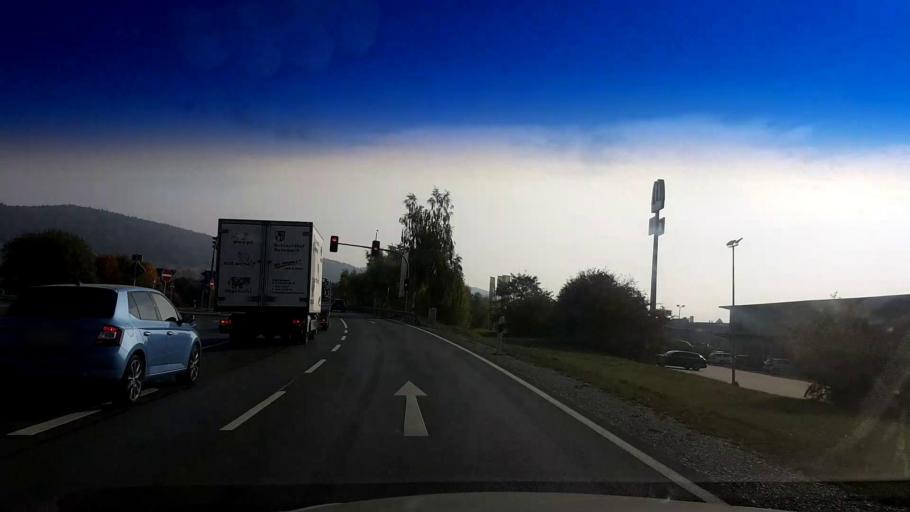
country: DE
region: Bavaria
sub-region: Upper Franconia
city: Himmelkron
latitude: 50.0552
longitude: 11.6152
